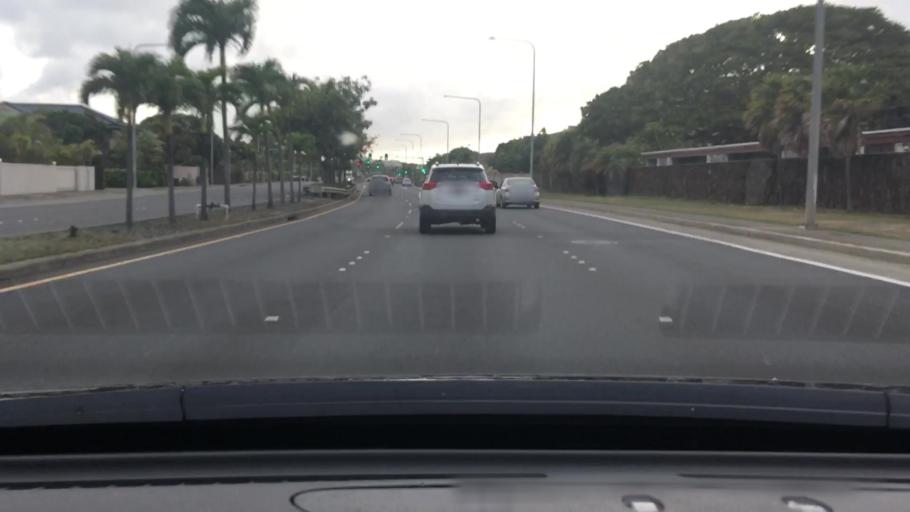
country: US
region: Hawaii
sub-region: Honolulu County
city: Waimanalo Beach
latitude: 21.2825
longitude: -157.7330
